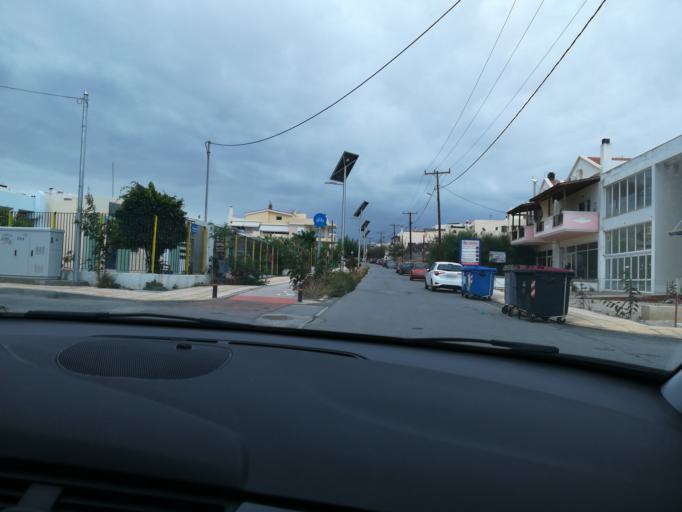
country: GR
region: Crete
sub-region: Nomos Lasithiou
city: Siteia
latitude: 35.2044
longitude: 26.0985
